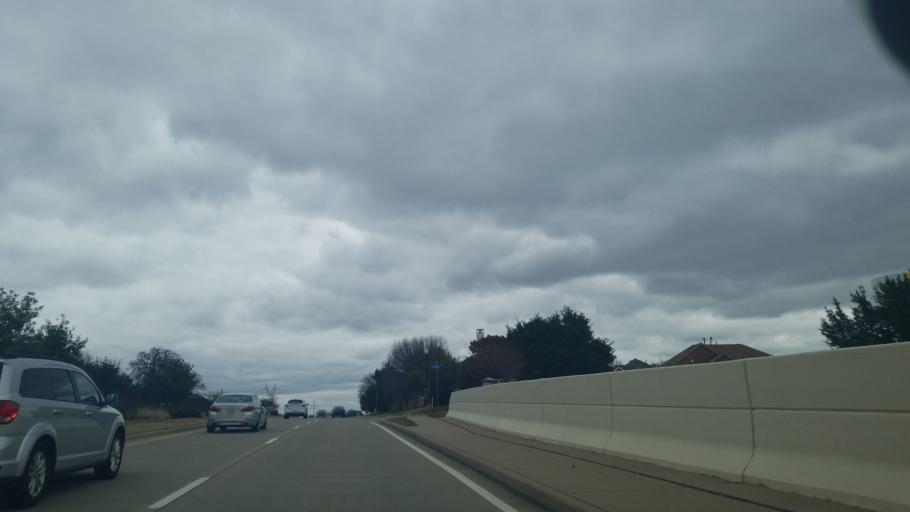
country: US
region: Texas
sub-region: Denton County
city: Copper Canyon
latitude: 33.0830
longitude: -97.0777
